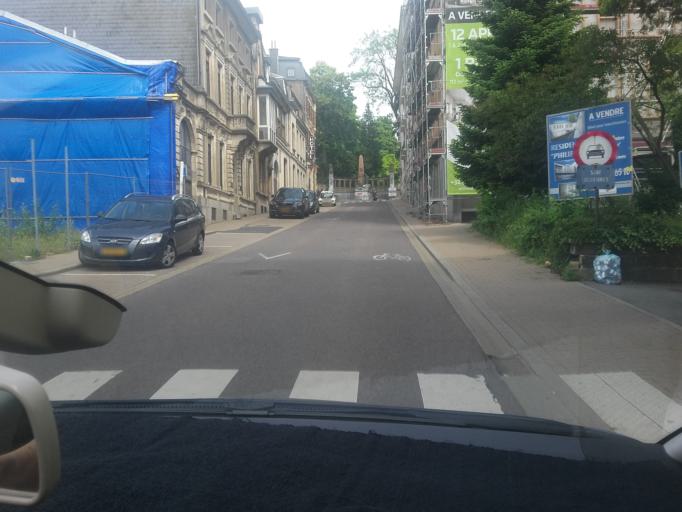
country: BE
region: Wallonia
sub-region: Province du Luxembourg
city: Arlon
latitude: 49.6815
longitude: 5.8120
